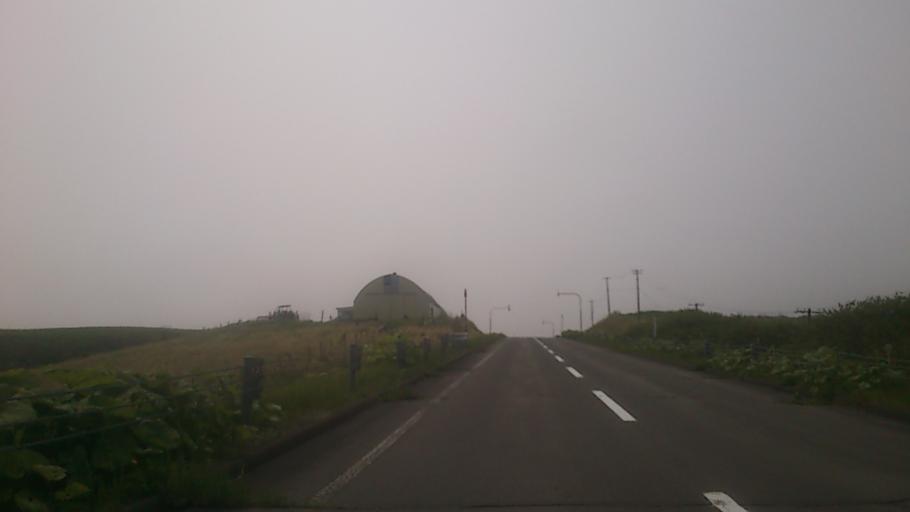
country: JP
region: Hokkaido
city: Nemuro
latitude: 43.1758
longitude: 145.3058
